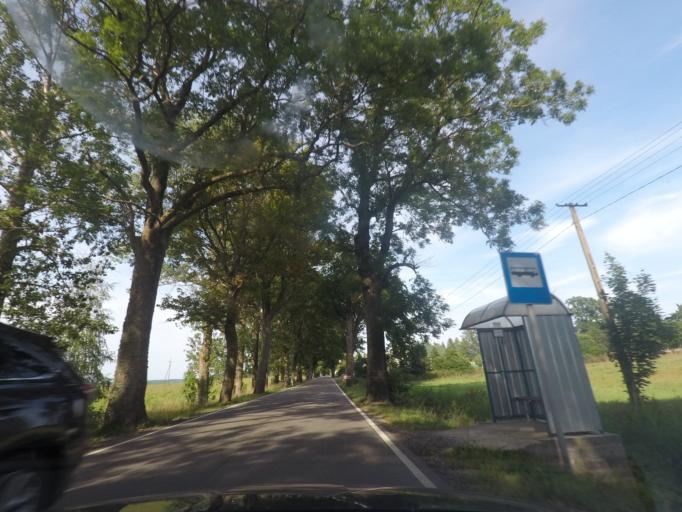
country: PL
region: Pomeranian Voivodeship
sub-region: Powiat leborski
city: Leba
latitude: 54.6386
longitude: 17.5311
